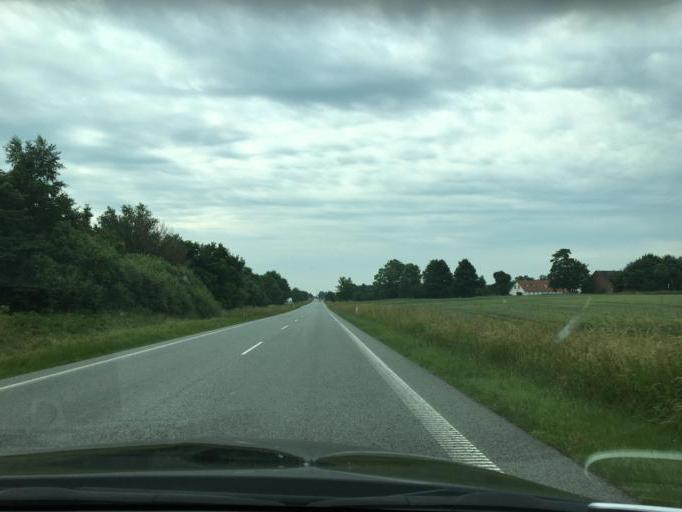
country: DK
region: South Denmark
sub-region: Kolding Kommune
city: Kolding
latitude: 55.6010
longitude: 9.4949
